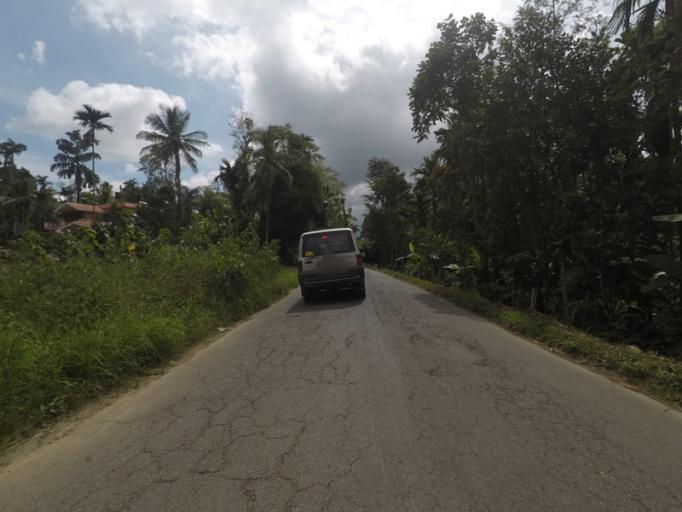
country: IN
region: Karnataka
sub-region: Kodagu
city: Virarajendrapet
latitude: 12.2312
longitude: 75.8387
